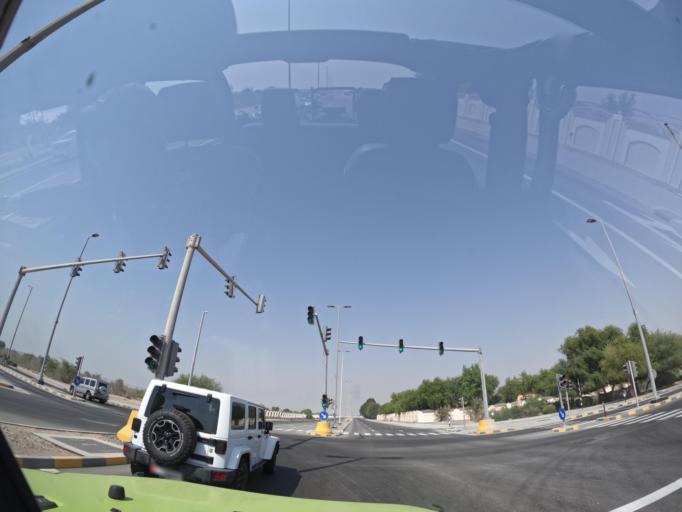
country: AE
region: Abu Dhabi
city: Abu Dhabi
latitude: 24.4725
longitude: 54.6304
